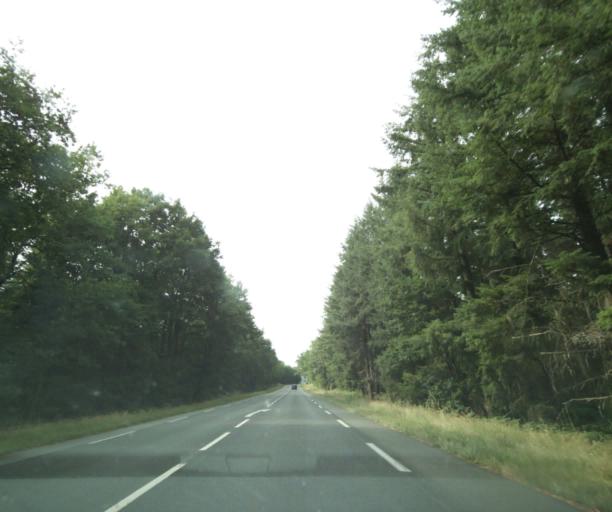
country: FR
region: Pays de la Loire
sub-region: Departement de la Sarthe
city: Marigne-Laille
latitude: 47.7701
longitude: 0.3492
